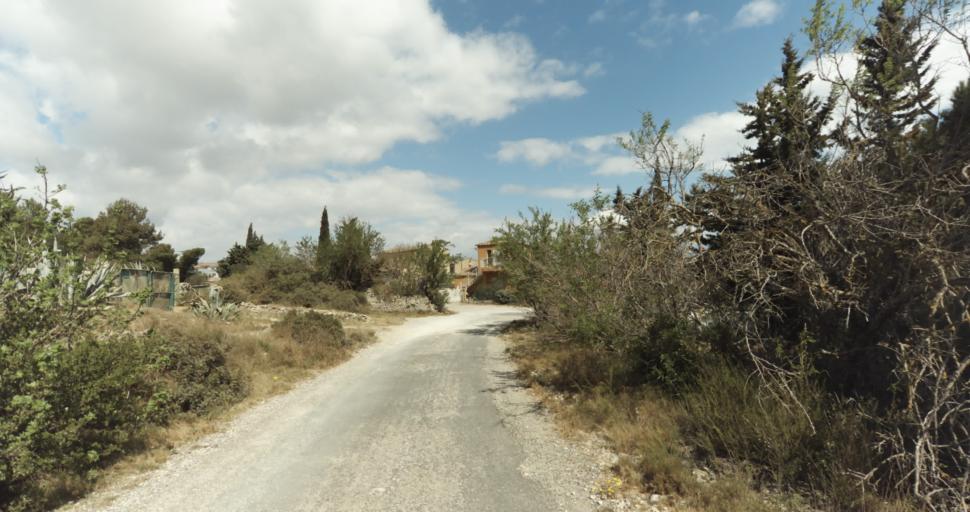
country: FR
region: Languedoc-Roussillon
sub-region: Departement de l'Aude
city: Leucate
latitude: 42.9030
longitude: 3.0309
